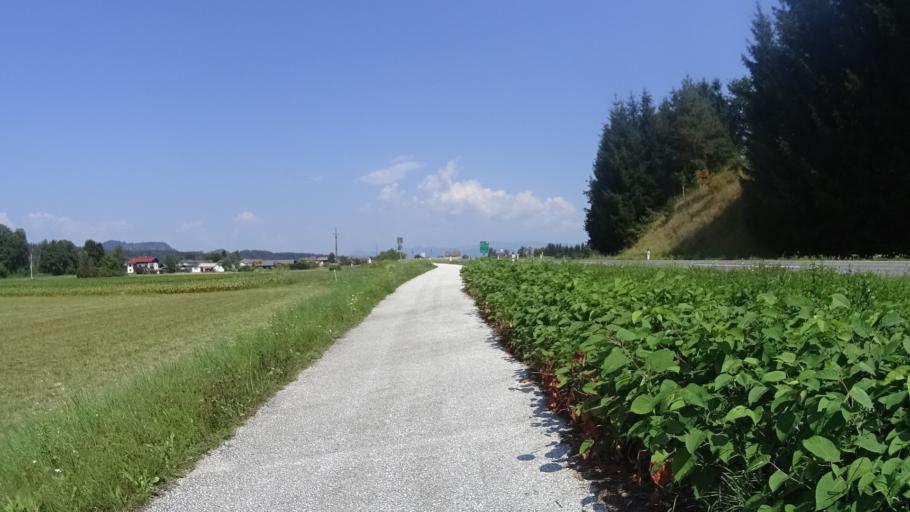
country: AT
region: Carinthia
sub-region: Politischer Bezirk Volkermarkt
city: Eberndorf
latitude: 46.5700
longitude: 14.6311
